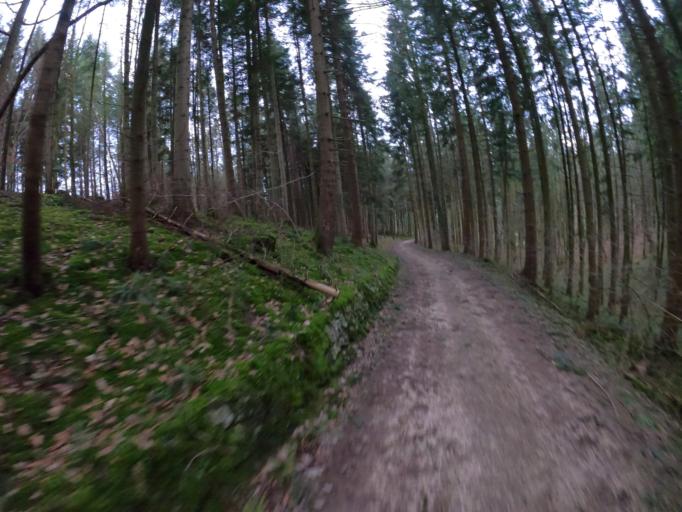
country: DE
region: Baden-Wuerttemberg
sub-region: Regierungsbezirk Stuttgart
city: Ottenbach
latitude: 48.7342
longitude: 9.7296
